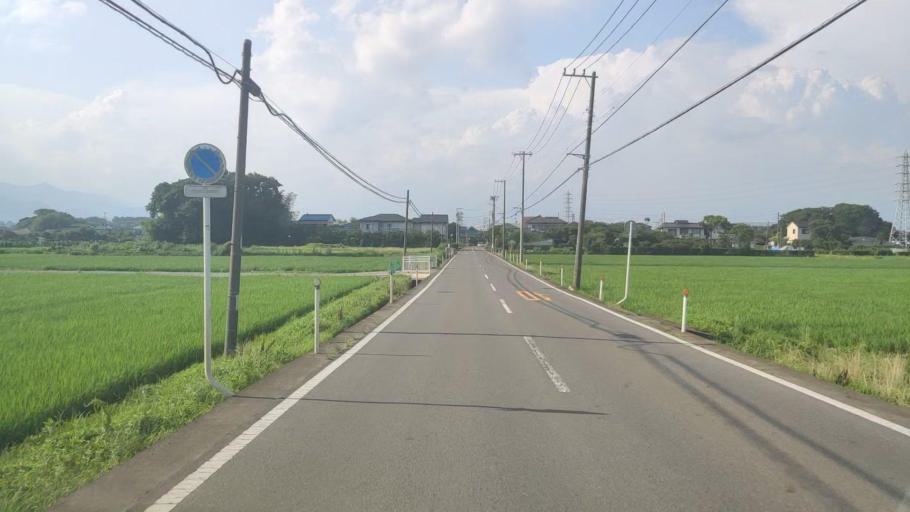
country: JP
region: Kanagawa
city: Isehara
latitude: 35.3686
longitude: 139.3285
